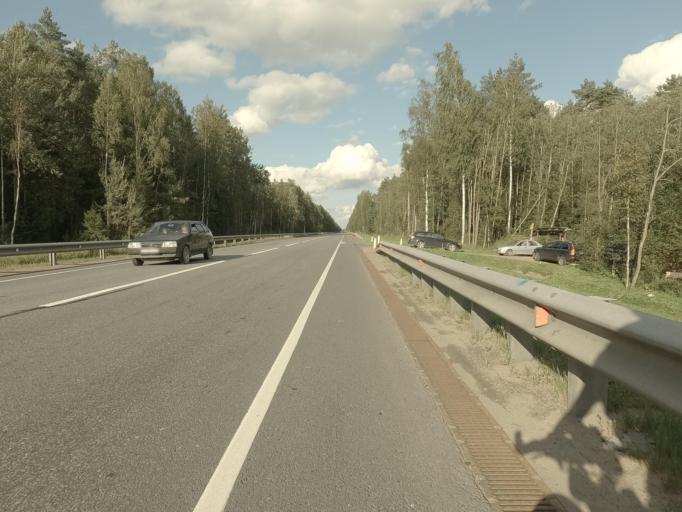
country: RU
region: Leningrad
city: Mga
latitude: 59.6954
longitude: 30.9862
